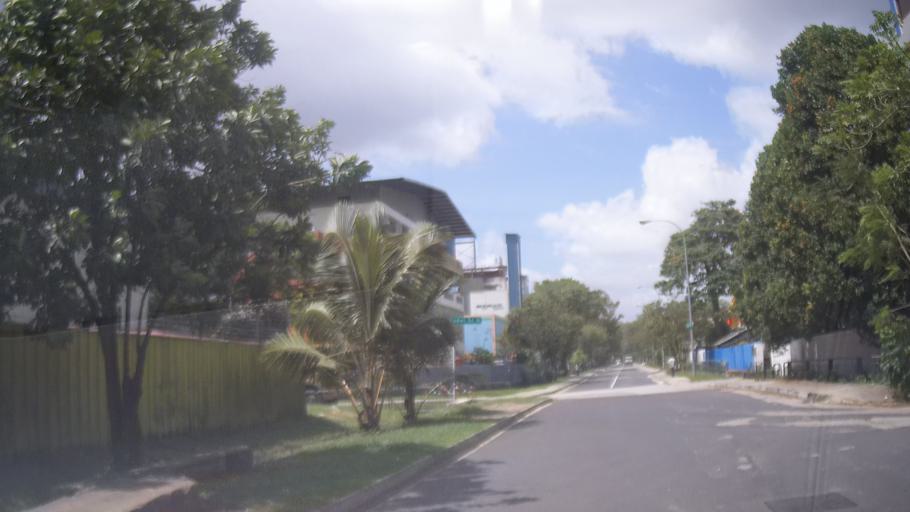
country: MY
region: Johor
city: Johor Bahru
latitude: 1.4294
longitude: 103.7508
